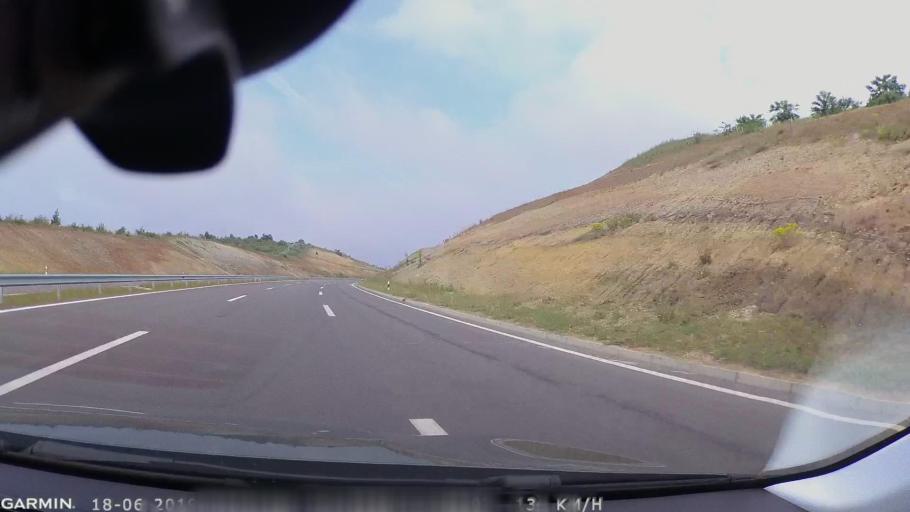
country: MK
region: Petrovec
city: Sredno Konjare
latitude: 41.9454
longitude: 21.7829
